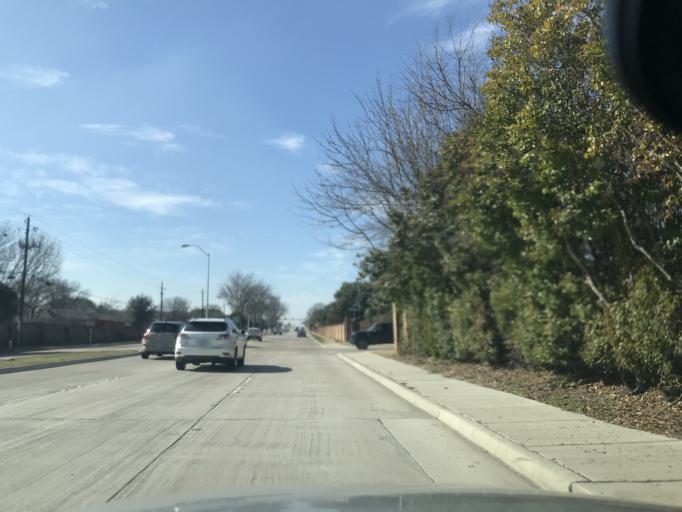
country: US
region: Texas
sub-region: Collin County
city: Plano
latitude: 33.0412
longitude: -96.7587
